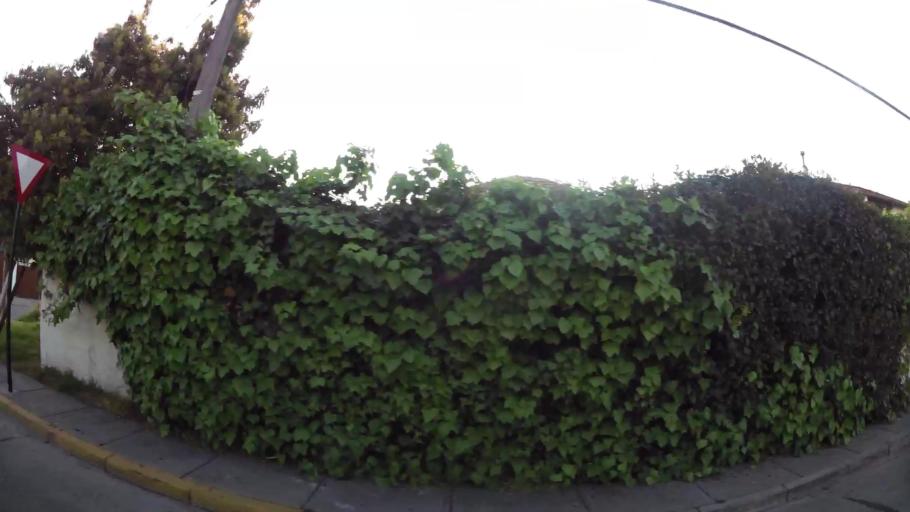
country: CL
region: Santiago Metropolitan
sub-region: Provincia de Santiago
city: Villa Presidente Frei, Nunoa, Santiago, Chile
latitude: -33.4027
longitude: -70.5581
